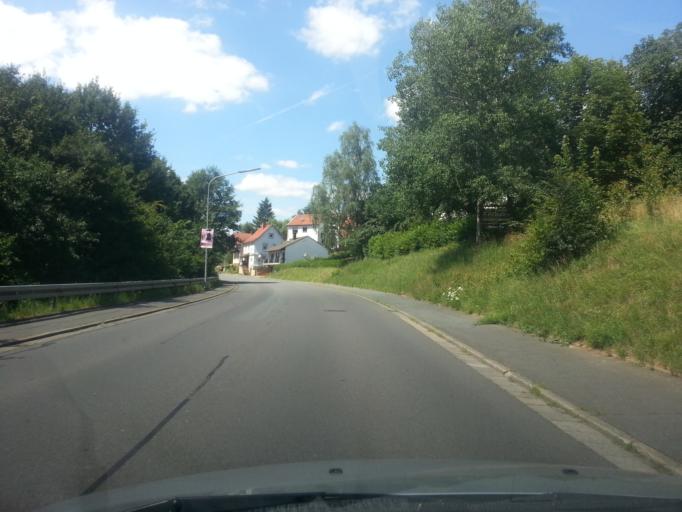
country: DE
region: Hesse
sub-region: Regierungsbezirk Darmstadt
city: Bad Konig
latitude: 49.7271
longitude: 8.9698
